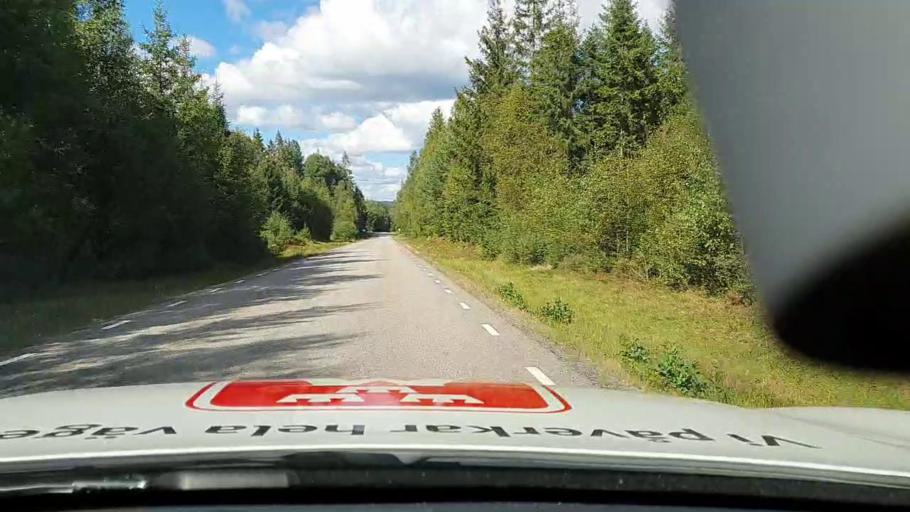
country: SE
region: Vaestra Goetaland
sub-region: Marks Kommun
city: Fritsla
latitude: 57.3907
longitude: 12.8536
